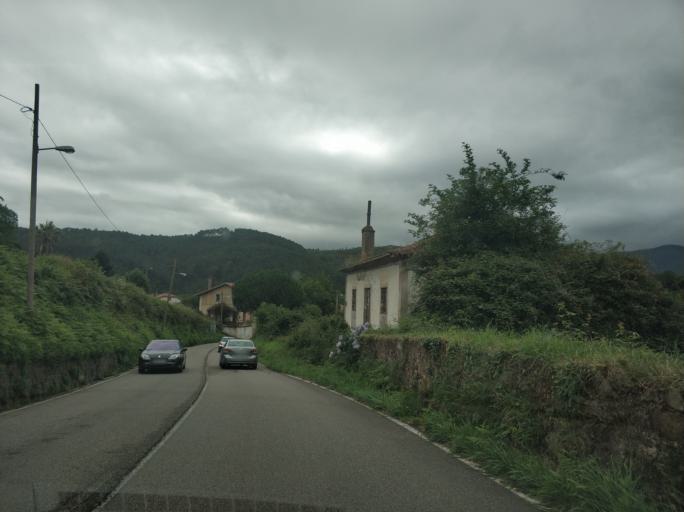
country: ES
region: Asturias
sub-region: Province of Asturias
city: Cudillero
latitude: 43.5637
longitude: -6.2339
